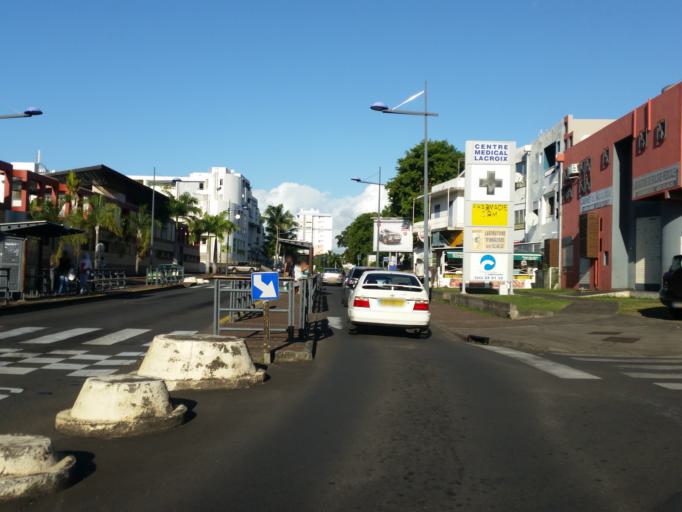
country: RE
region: Reunion
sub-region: Reunion
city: Saint-Denis
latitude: -20.8931
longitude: 55.4841
